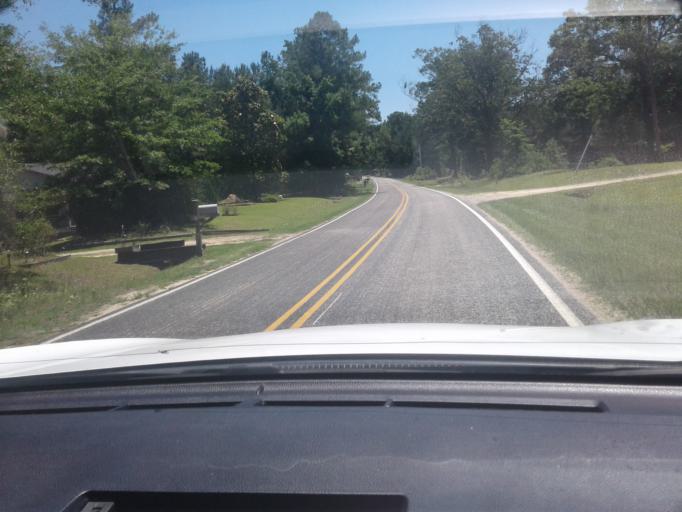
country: US
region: North Carolina
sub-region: Harnett County
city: Lillington
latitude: 35.3511
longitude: -78.9117
